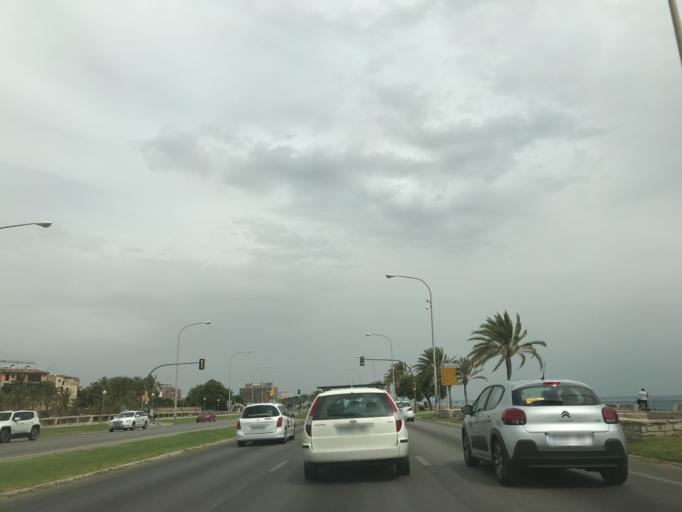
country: ES
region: Balearic Islands
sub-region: Illes Balears
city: Palma
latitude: 39.5649
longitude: 2.6490
